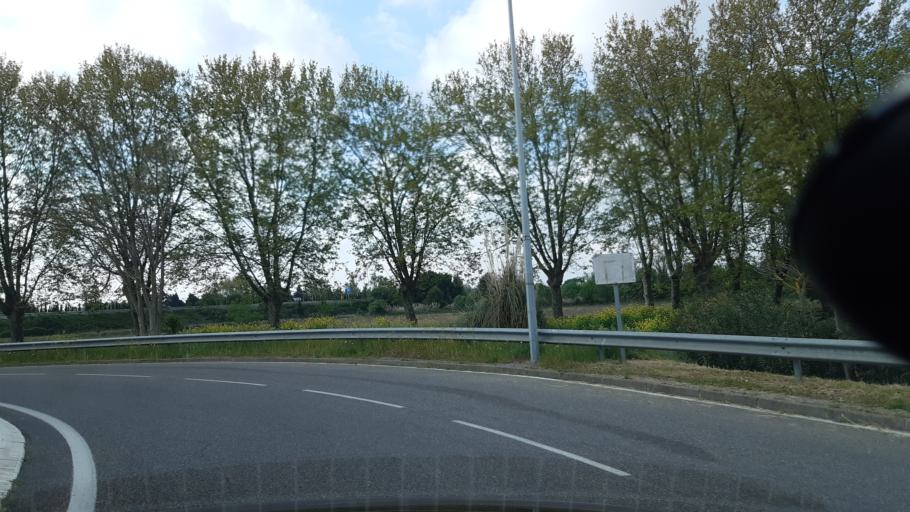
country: FR
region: Languedoc-Roussillon
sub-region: Departement de l'Aude
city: Narbonne
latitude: 43.1757
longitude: 3.0259
